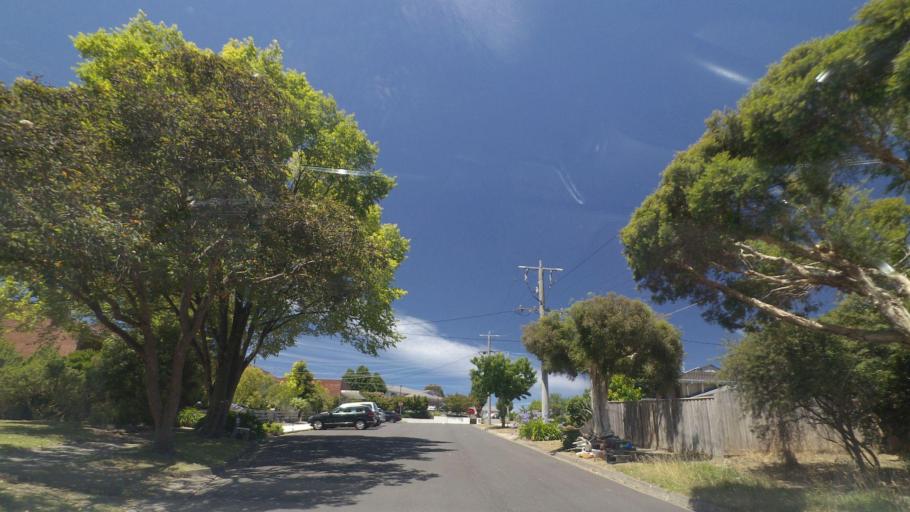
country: AU
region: Victoria
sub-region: Maroondah
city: Croydon North
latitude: -37.7809
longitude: 145.3162
